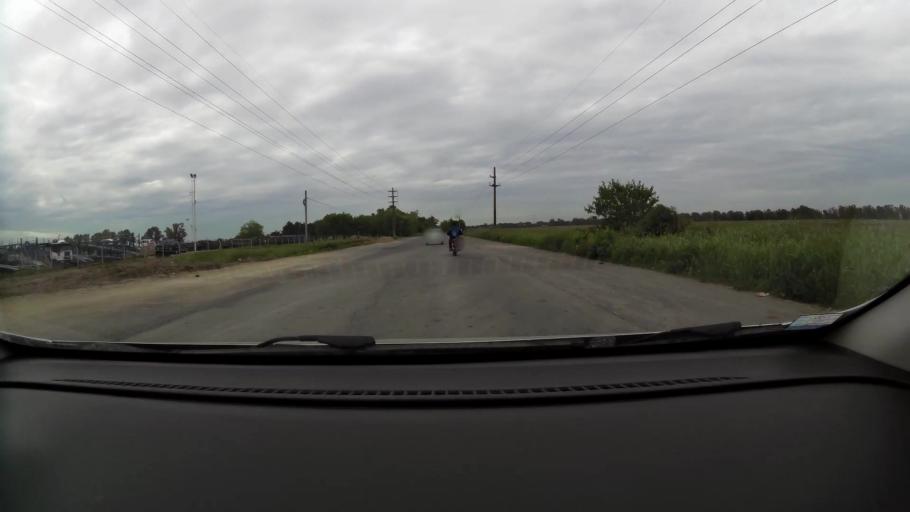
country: AR
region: Buenos Aires
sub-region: Partido de Zarate
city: Zarate
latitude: -34.1060
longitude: -59.0991
